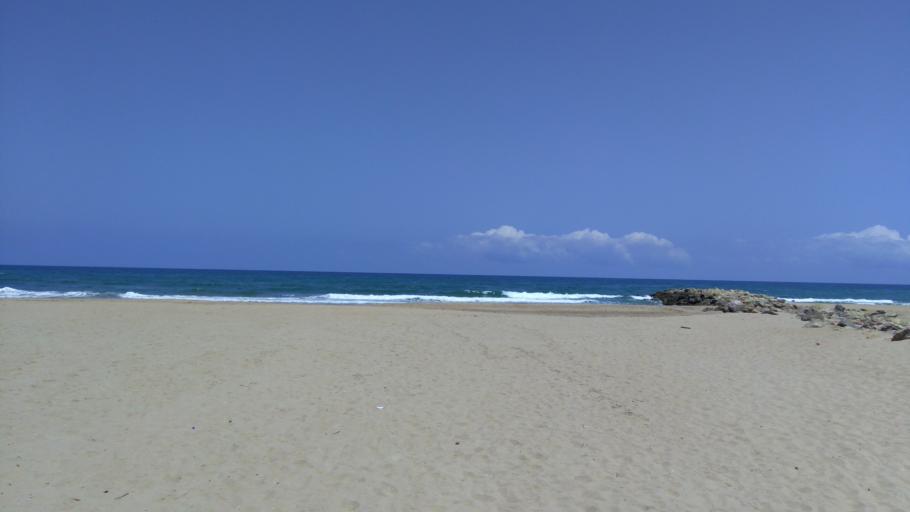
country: ES
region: Valencia
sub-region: Provincia de Valencia
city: Xeraco,Jaraco
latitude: 39.0583
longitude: -0.1997
